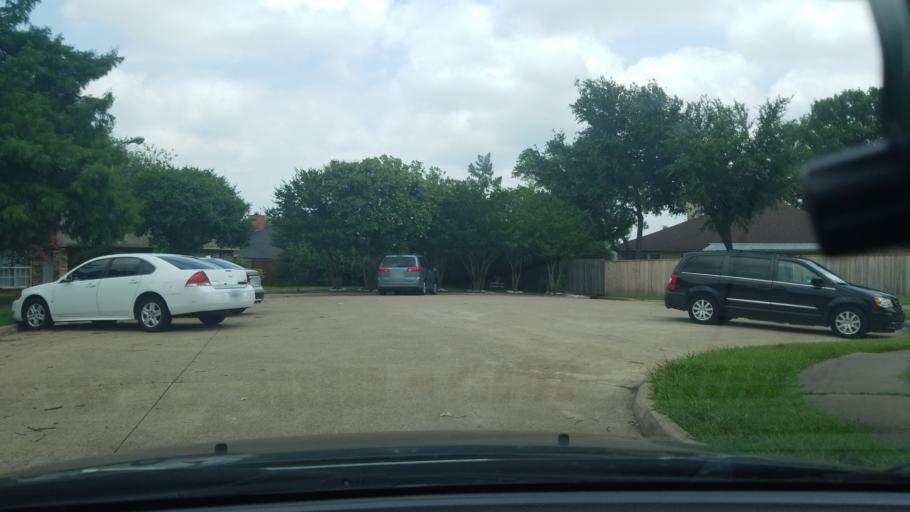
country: US
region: Texas
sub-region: Dallas County
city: Mesquite
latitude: 32.8003
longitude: -96.6163
